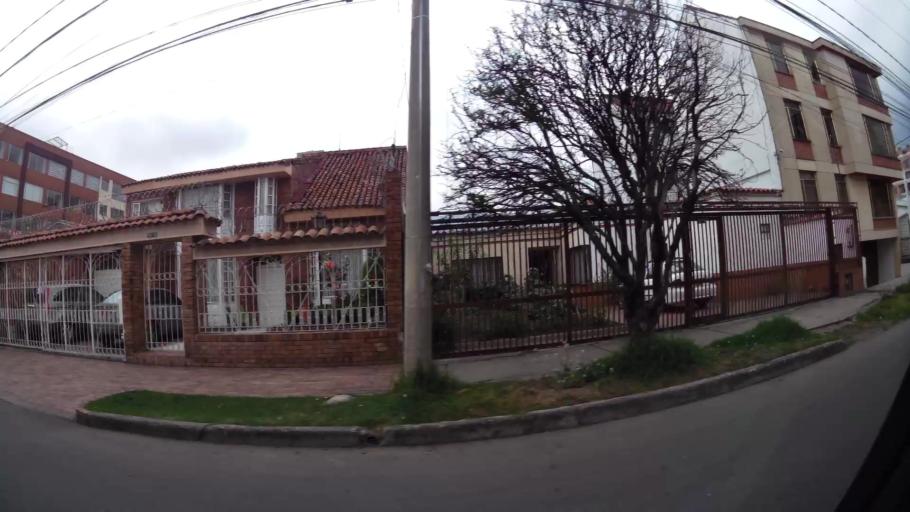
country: CO
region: Bogota D.C.
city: Barrio San Luis
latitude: 4.7172
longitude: -74.0412
